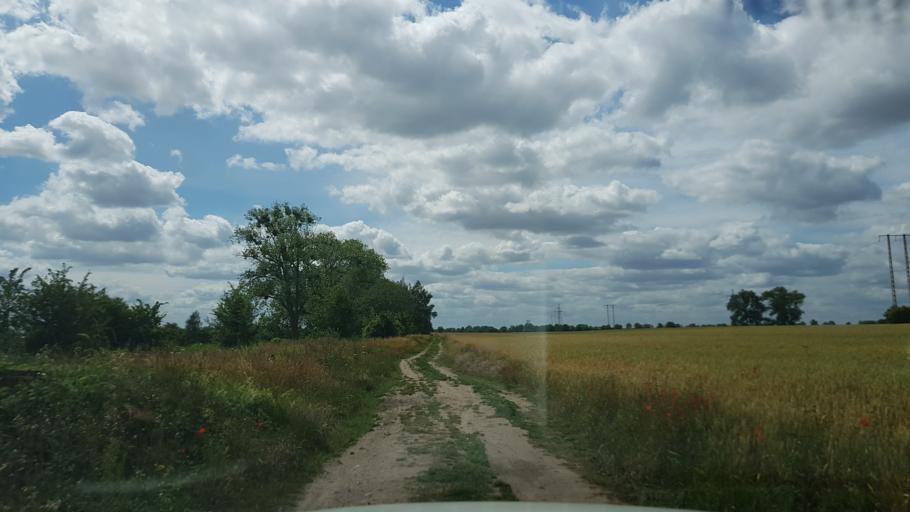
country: PL
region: West Pomeranian Voivodeship
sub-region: Powiat pyrzycki
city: Lipiany
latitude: 52.9644
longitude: 14.9854
